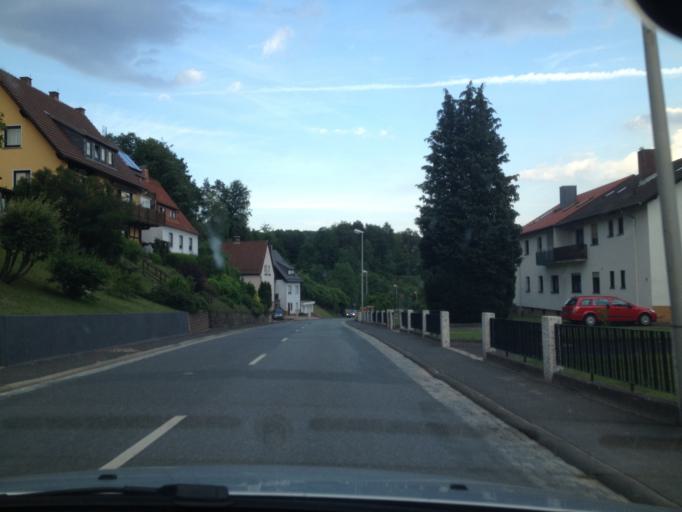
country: DE
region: Bavaria
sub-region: Regierungsbezirk Unterfranken
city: Weibersbrunn
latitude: 49.9350
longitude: 9.3575
